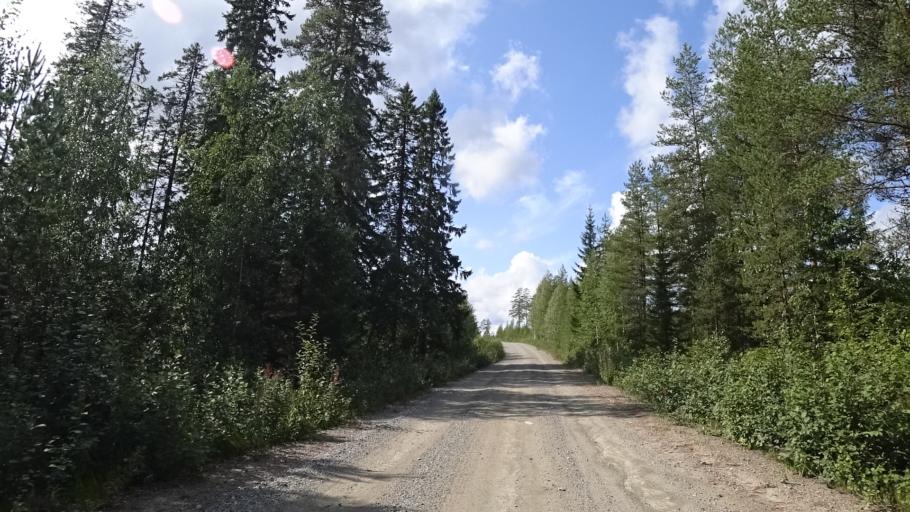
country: FI
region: North Karelia
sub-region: Joensuu
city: Ilomantsi
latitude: 62.9269
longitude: 31.3789
